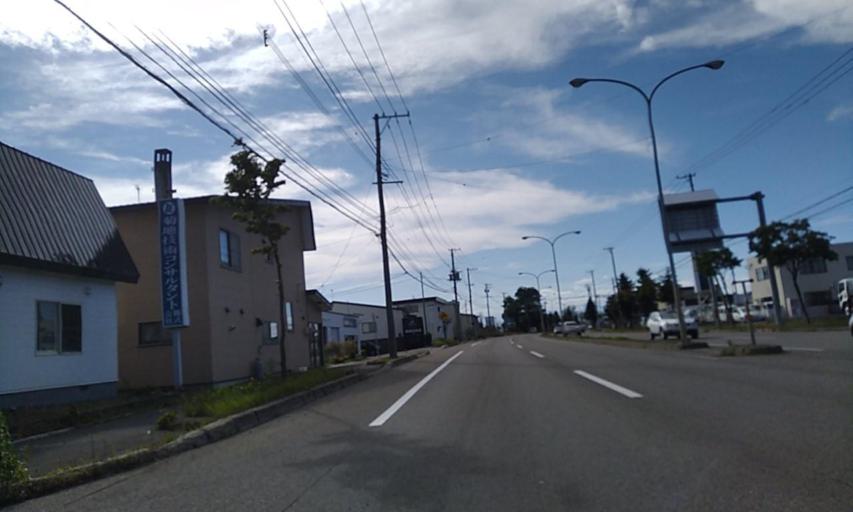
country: JP
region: Hokkaido
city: Obihiro
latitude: 42.9155
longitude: 143.2541
